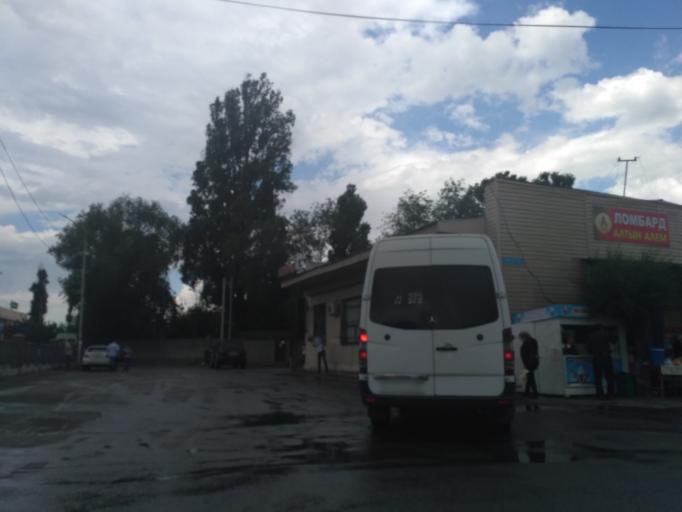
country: KZ
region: Almaty Oblysy
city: Burunday
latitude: 43.2001
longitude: 76.6339
